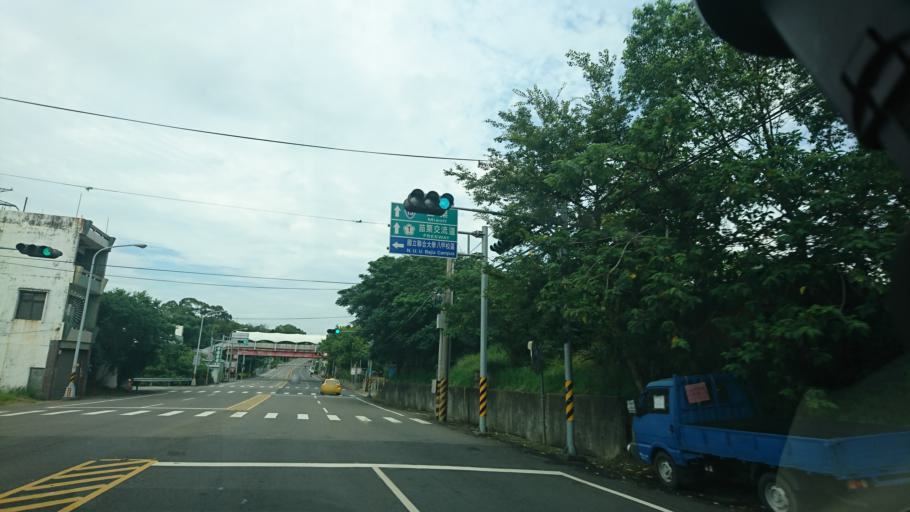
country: TW
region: Taiwan
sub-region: Miaoli
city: Miaoli
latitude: 24.5266
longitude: 120.7973
